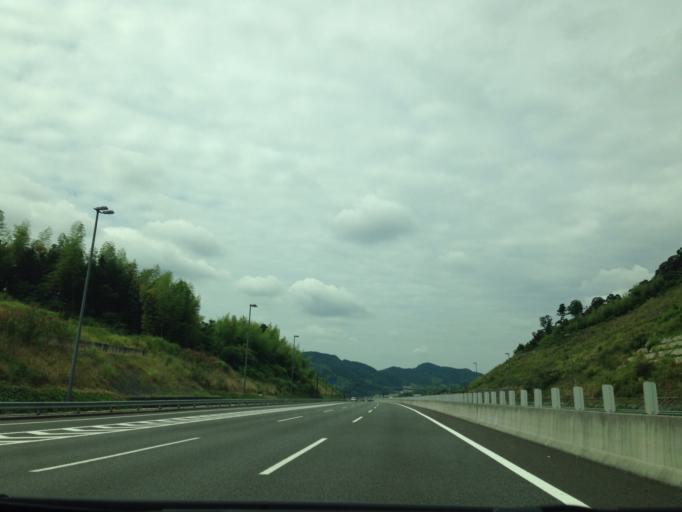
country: JP
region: Shizuoka
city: Fujieda
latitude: 34.9116
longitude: 138.2557
